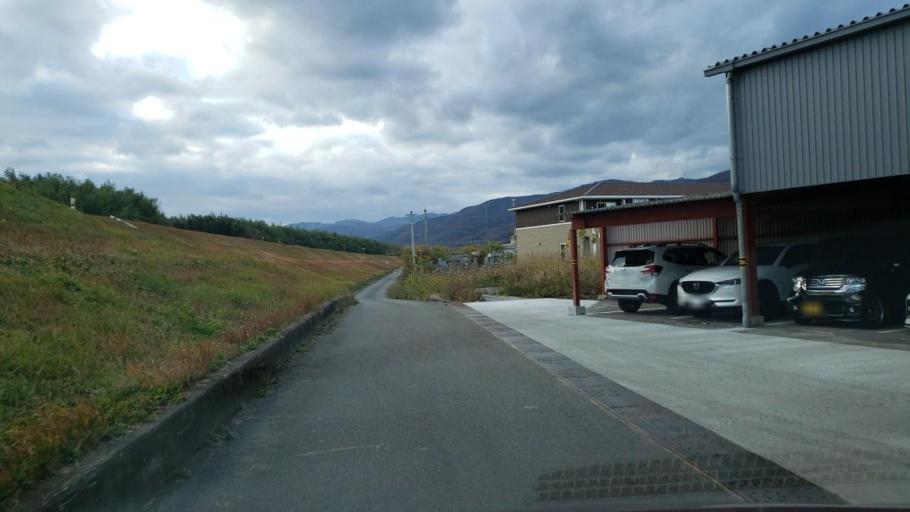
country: JP
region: Tokushima
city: Wakimachi
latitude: 34.0617
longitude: 134.1619
